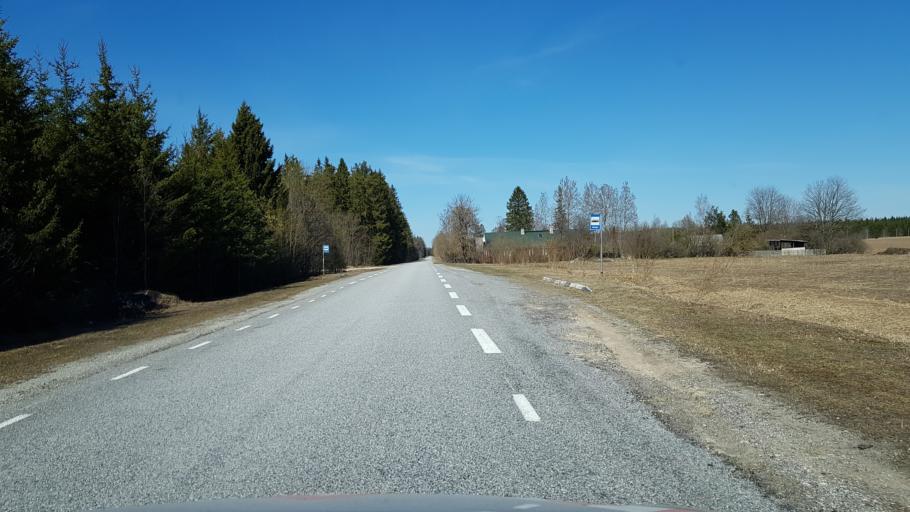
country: EE
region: Laeaene-Virumaa
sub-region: Vinni vald
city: Vinni
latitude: 59.1604
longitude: 26.5131
